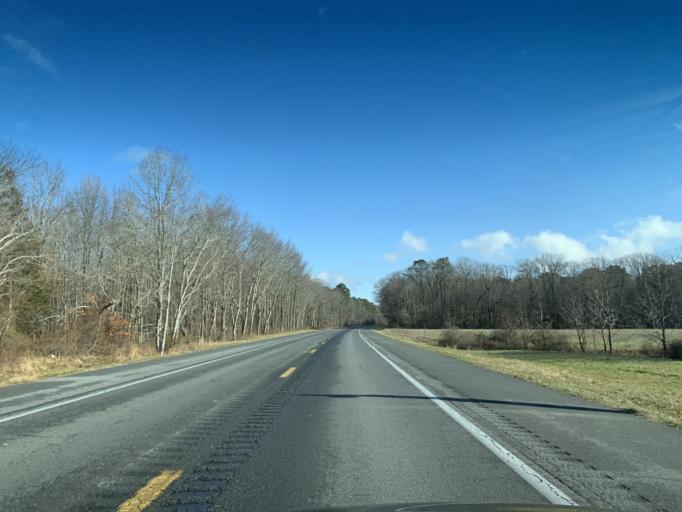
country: US
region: Maryland
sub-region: Worcester County
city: Berlin
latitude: 38.3765
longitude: -75.2406
